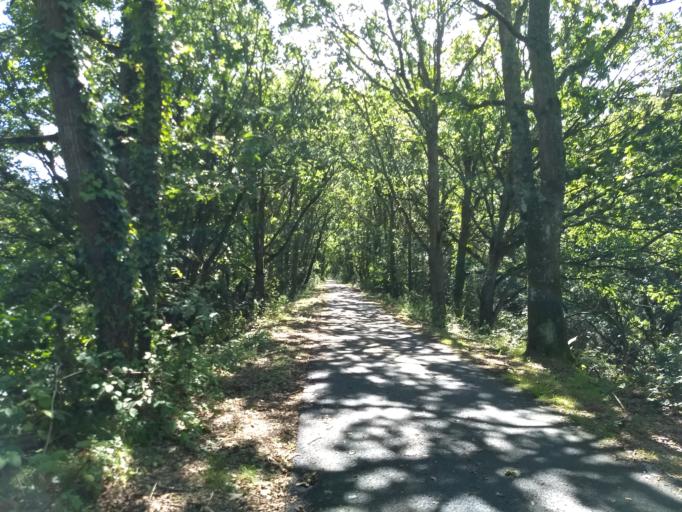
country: GB
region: England
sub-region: Isle of Wight
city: East Cowes
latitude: 50.7375
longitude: -1.2898
